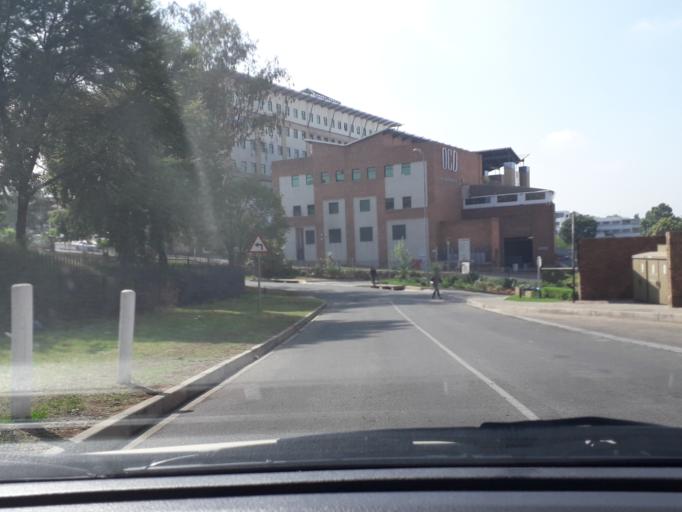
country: ZA
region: Gauteng
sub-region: City of Johannesburg Metropolitan Municipality
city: Midrand
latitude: -26.0352
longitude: 28.0636
